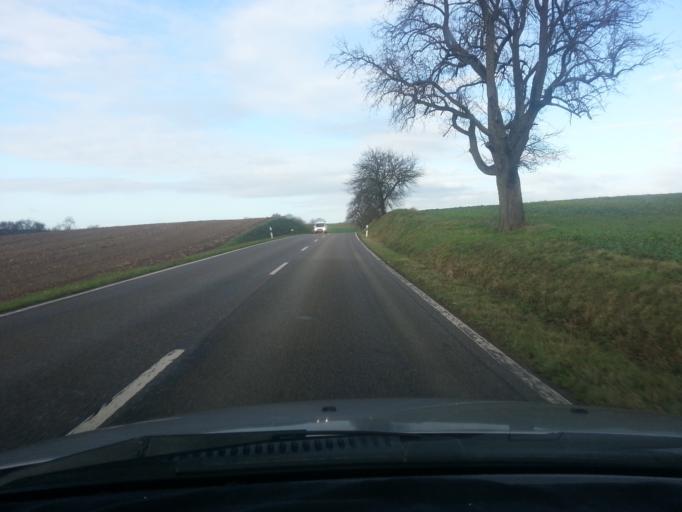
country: DE
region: Baden-Wuerttemberg
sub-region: Karlsruhe Region
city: Sulzfeld
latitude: 49.1659
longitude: 8.8578
